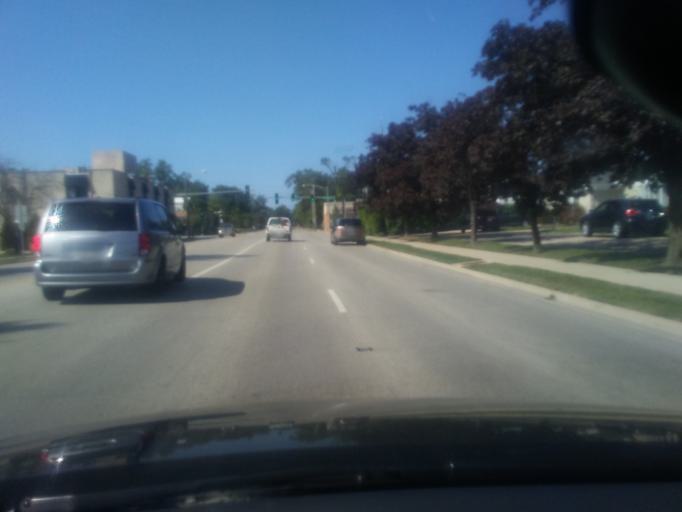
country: US
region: Illinois
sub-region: Cook County
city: Skokie
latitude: 42.0471
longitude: -87.7276
